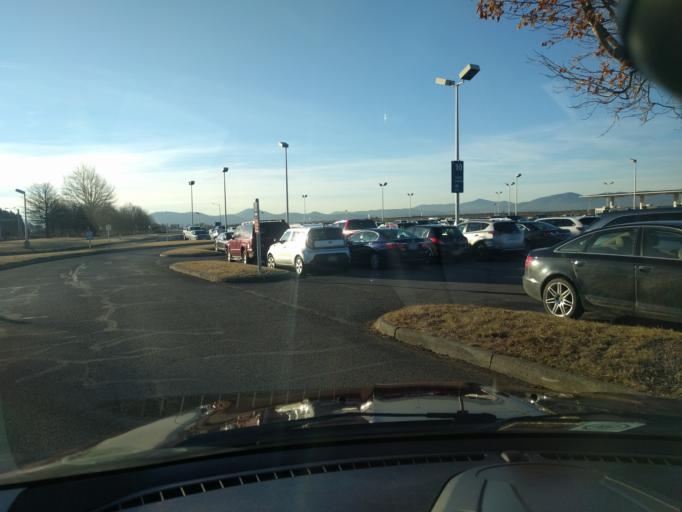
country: US
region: Virginia
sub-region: Roanoke County
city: Hollins
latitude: 37.3190
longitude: -79.9693
